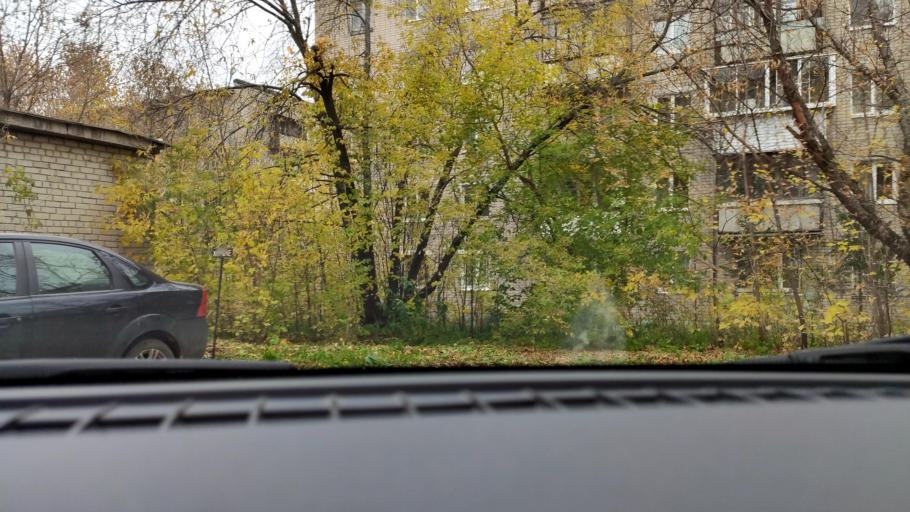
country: RU
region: Perm
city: Perm
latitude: 58.0023
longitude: 56.2765
